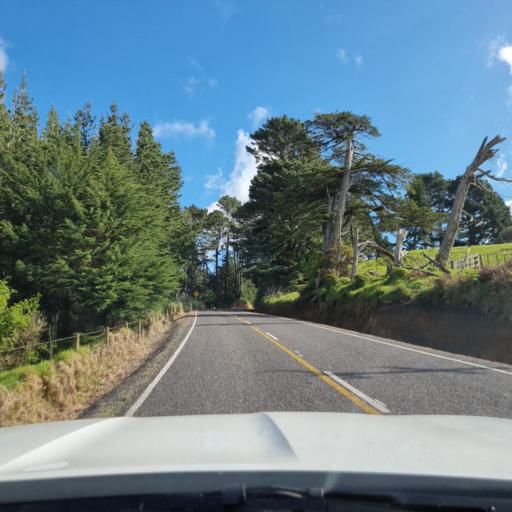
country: NZ
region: Northland
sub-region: Kaipara District
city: Dargaville
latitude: -36.2821
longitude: 174.0837
